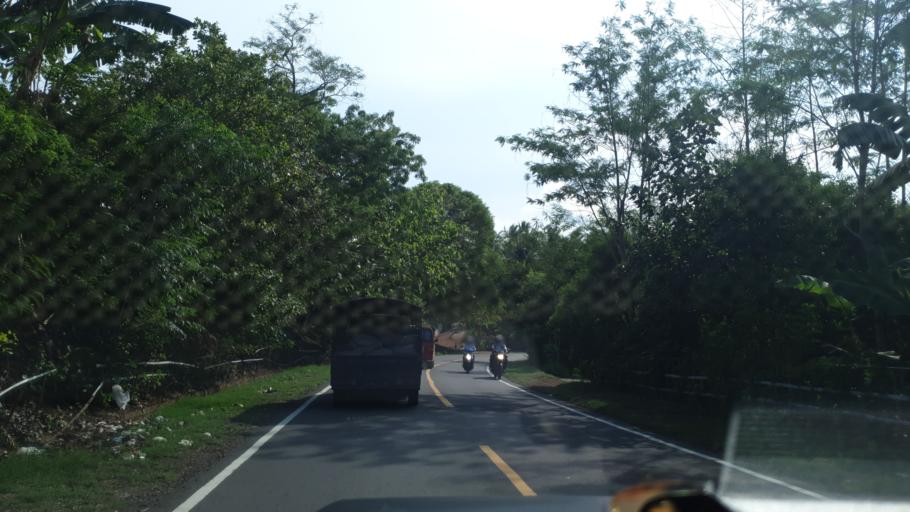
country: ID
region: East Nusa Tenggara
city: Nangalimang
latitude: -8.6616
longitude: 122.1946
